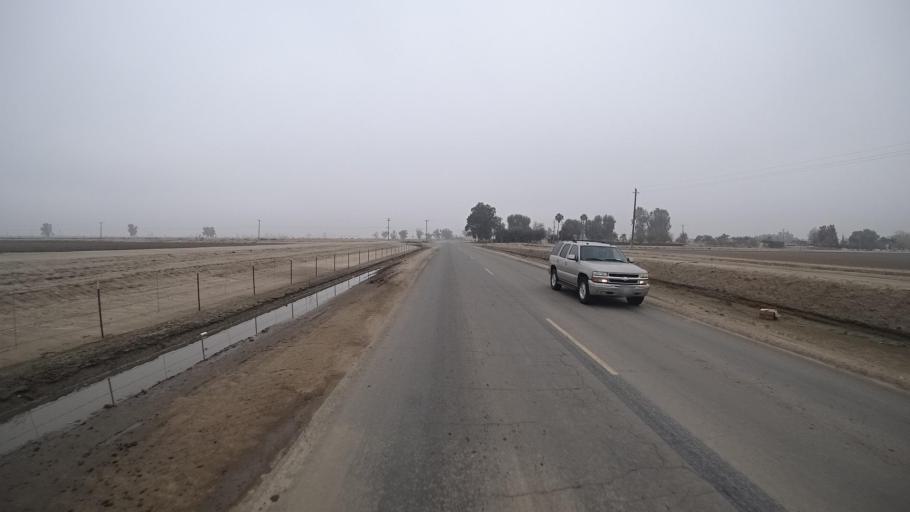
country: US
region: California
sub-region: Kern County
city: Greenfield
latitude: 35.2372
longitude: -119.0226
